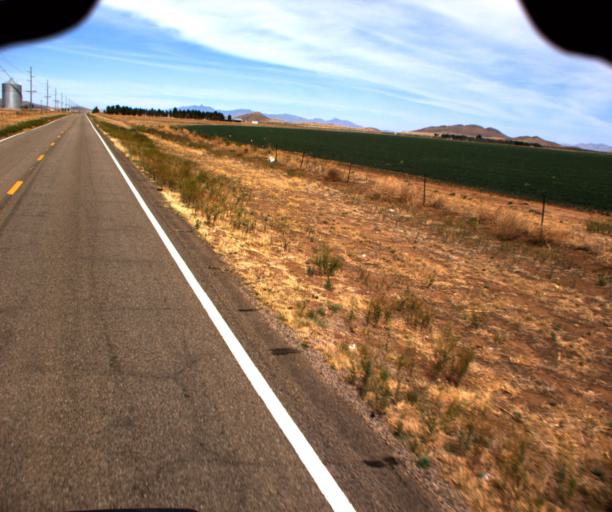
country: US
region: Arizona
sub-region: Cochise County
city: Tombstone
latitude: 31.8212
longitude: -109.6951
